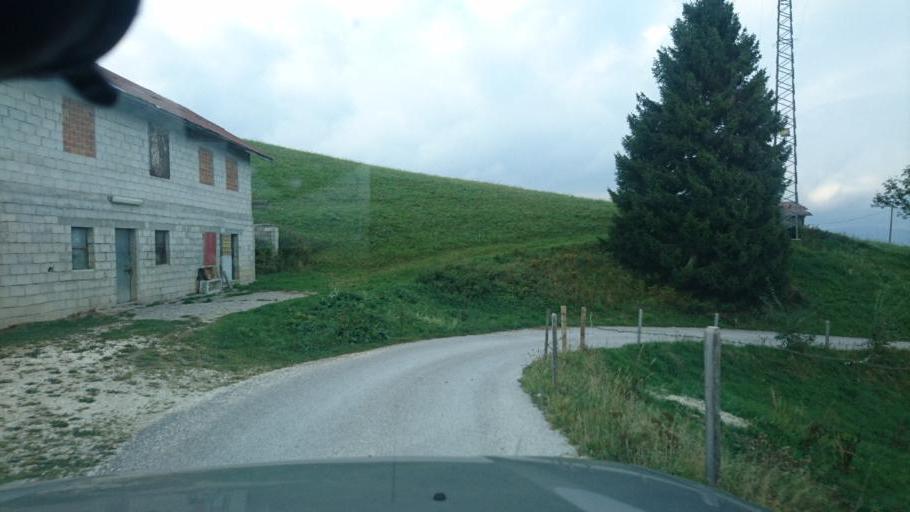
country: IT
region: Veneto
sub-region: Provincia di Vicenza
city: Enego
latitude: 45.9456
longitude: 11.6802
